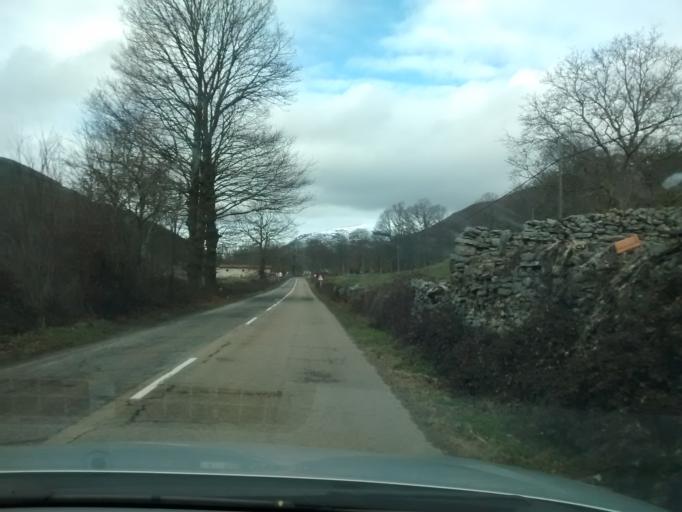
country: ES
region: Castille and Leon
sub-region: Provincia de Burgos
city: Espinosa de los Monteros
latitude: 43.0926
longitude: -3.5609
